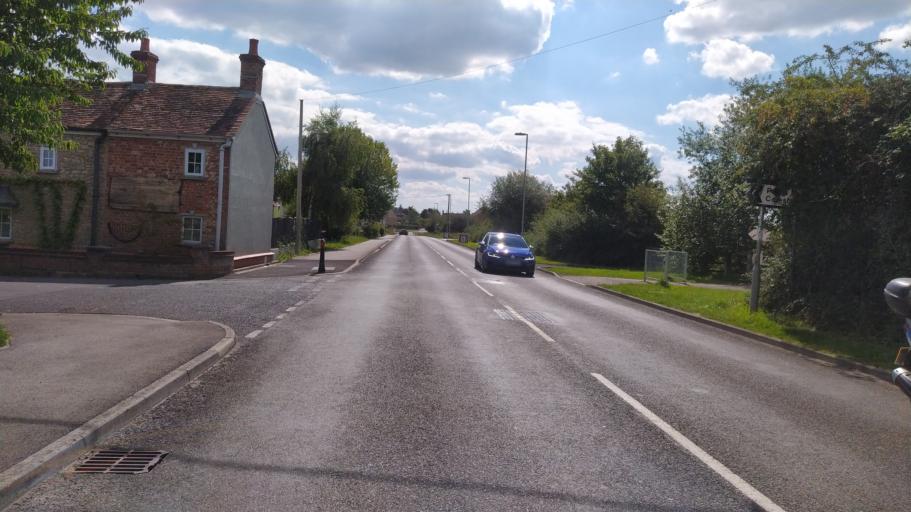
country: GB
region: England
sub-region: Dorset
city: Gillingham
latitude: 51.0505
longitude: -2.2821
